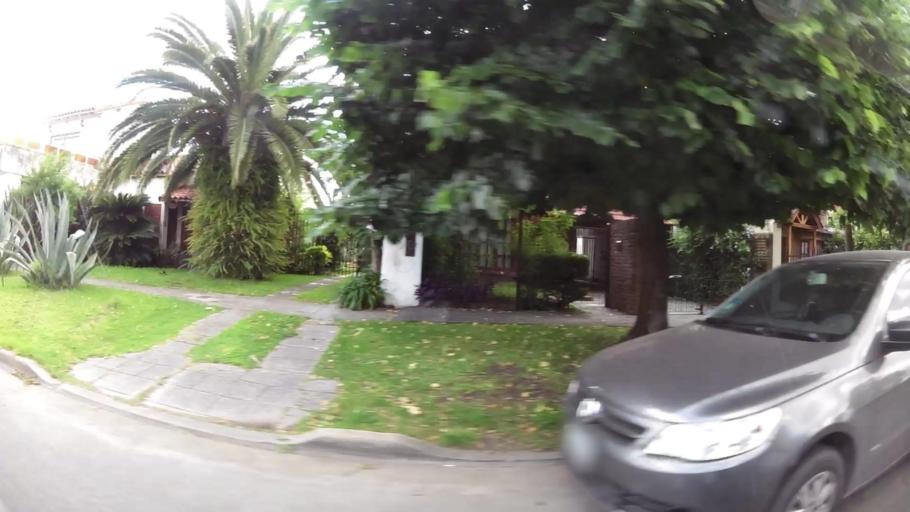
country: AR
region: Buenos Aires
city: Ituzaingo
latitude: -34.6430
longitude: -58.6599
